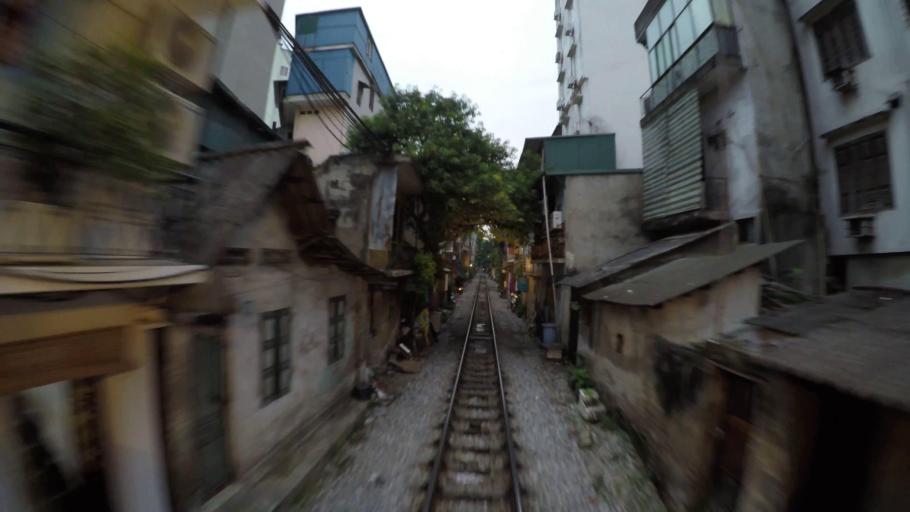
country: VN
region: Ha Noi
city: Hoan Kiem
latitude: 21.0377
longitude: 105.8463
